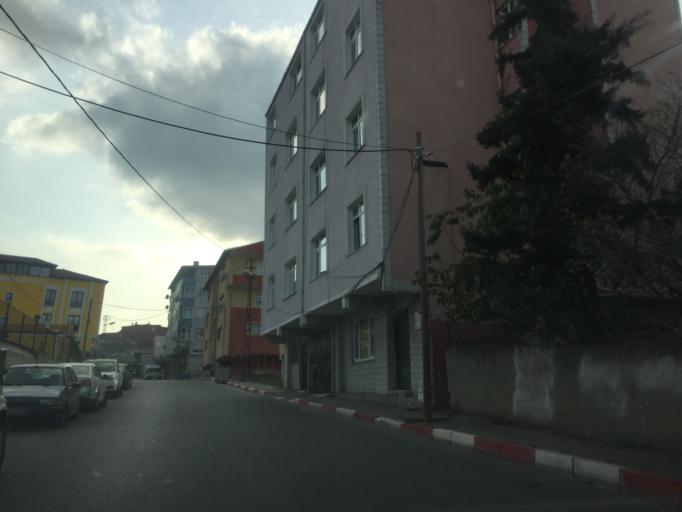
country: TR
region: Istanbul
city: Sultanbeyli
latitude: 40.9464
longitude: 29.2979
